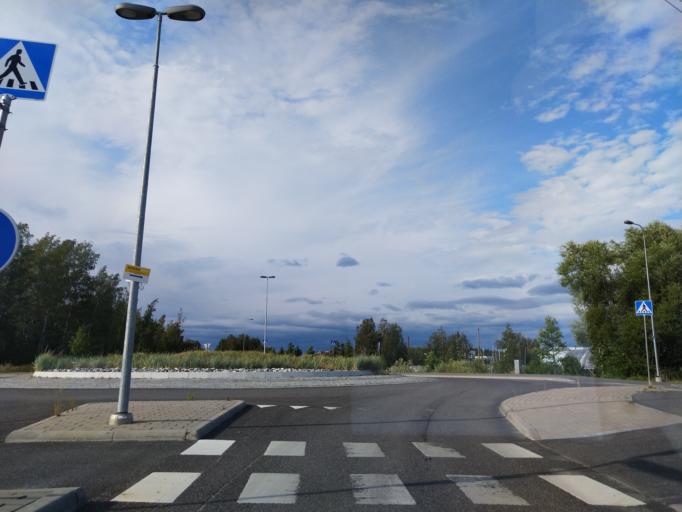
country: FI
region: Varsinais-Suomi
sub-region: Turku
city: Turku
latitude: 60.4214
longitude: 22.2276
